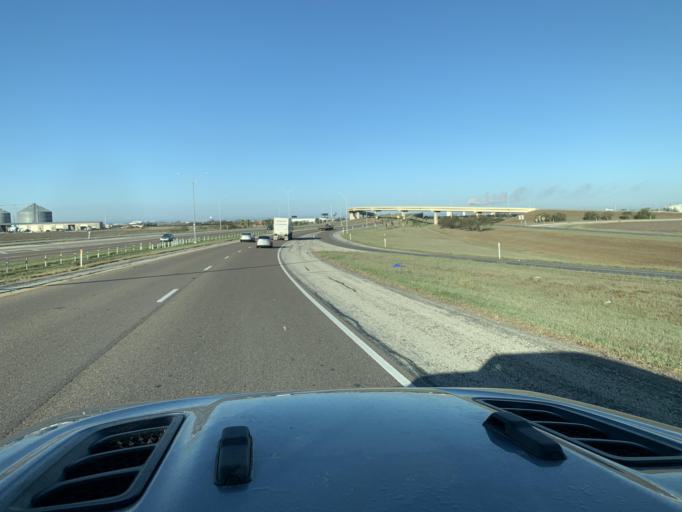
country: US
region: Texas
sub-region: Nueces County
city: Corpus Christi
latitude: 27.7819
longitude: -97.4799
